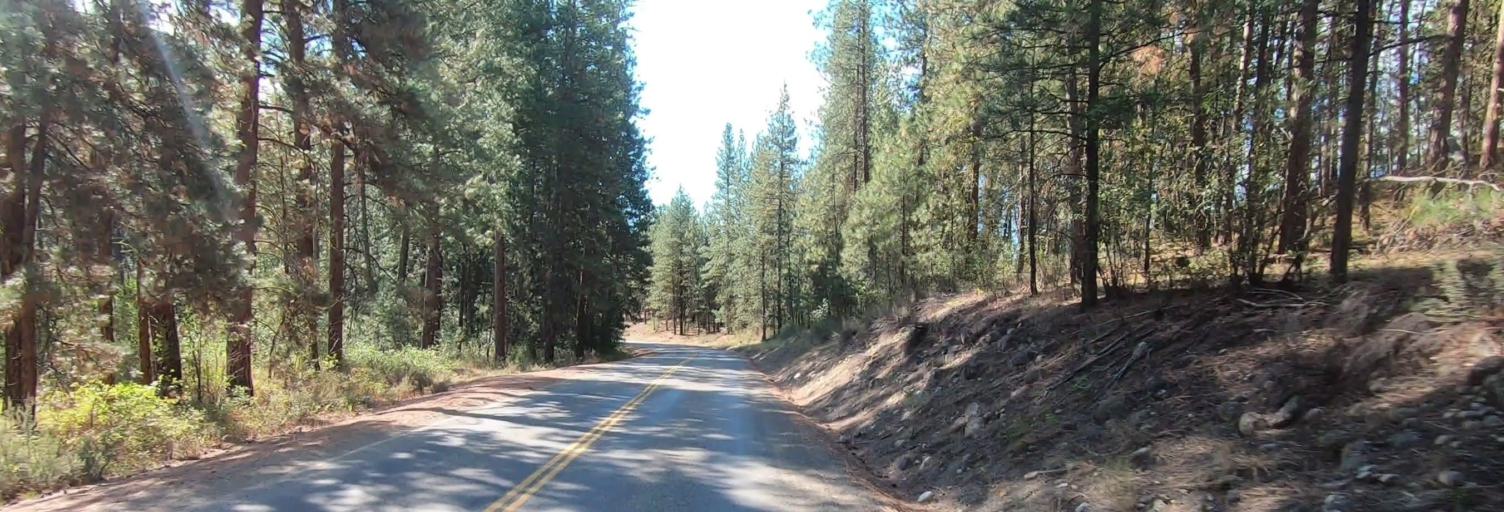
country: US
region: Washington
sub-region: Okanogan County
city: Brewster
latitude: 48.5419
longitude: -120.1796
